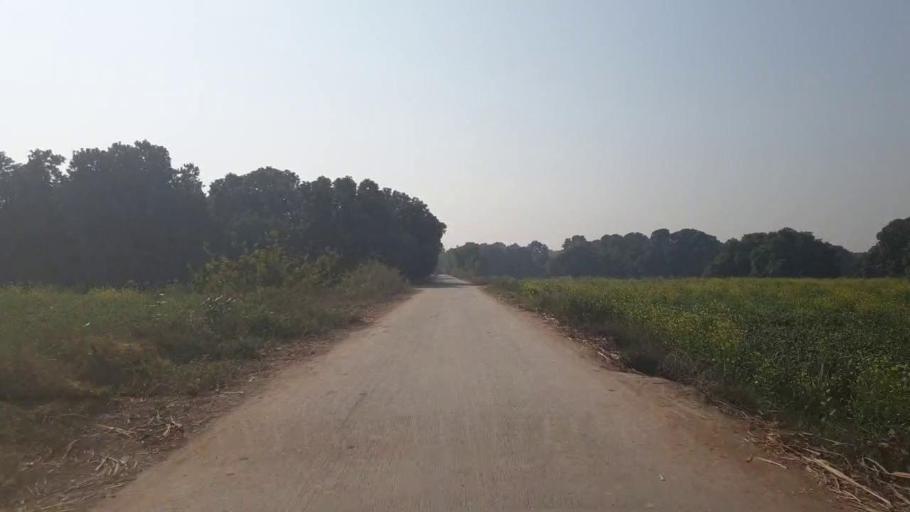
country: PK
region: Sindh
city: Tando Allahyar
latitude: 25.4691
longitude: 68.7754
